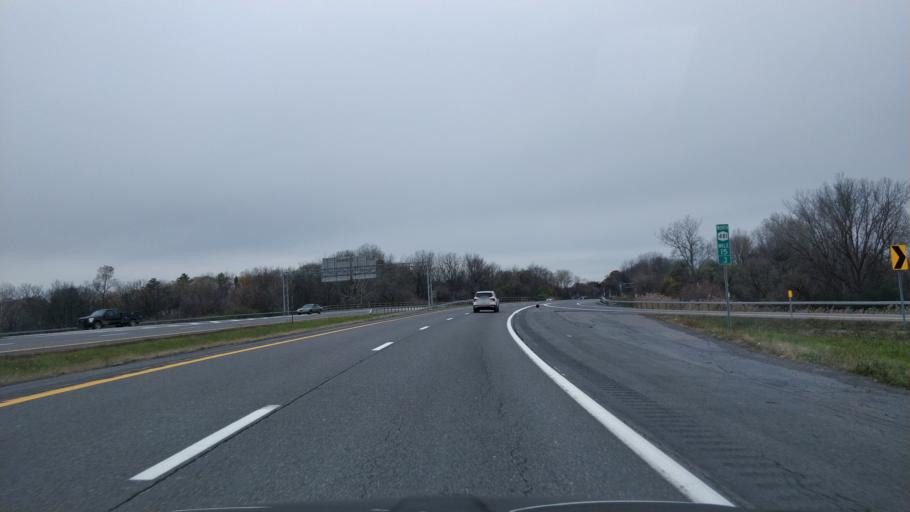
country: US
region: New York
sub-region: Onondaga County
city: North Syracuse
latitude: 43.1420
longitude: -76.1161
